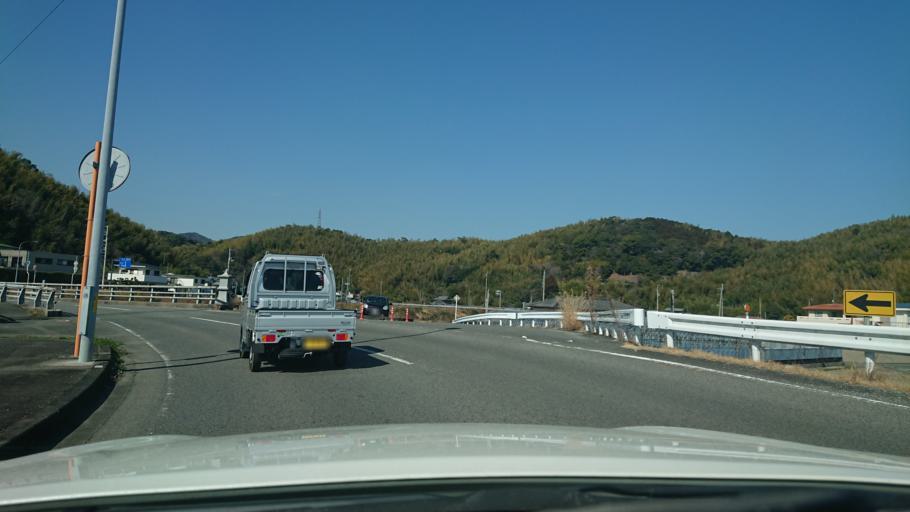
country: JP
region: Tokushima
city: Komatsushimacho
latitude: 33.9698
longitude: 134.6013
